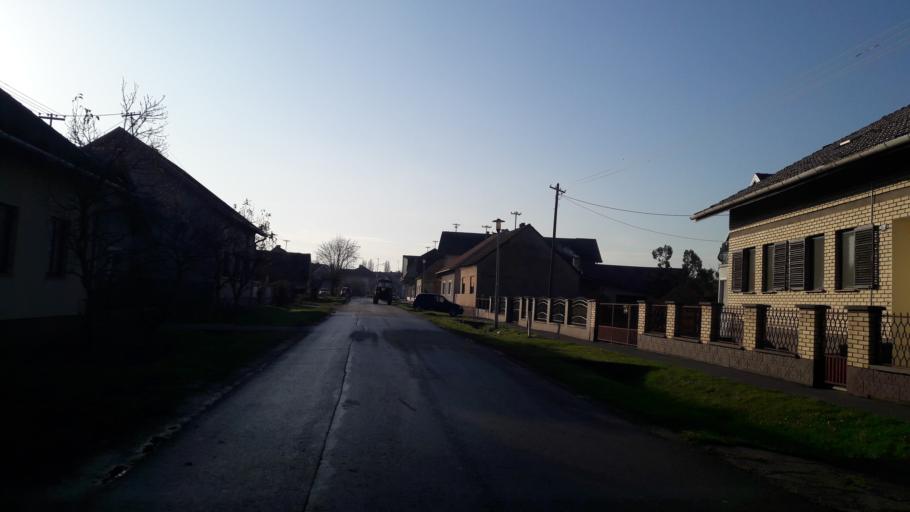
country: HR
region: Osjecko-Baranjska
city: Darda
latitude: 45.6258
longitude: 18.6912
